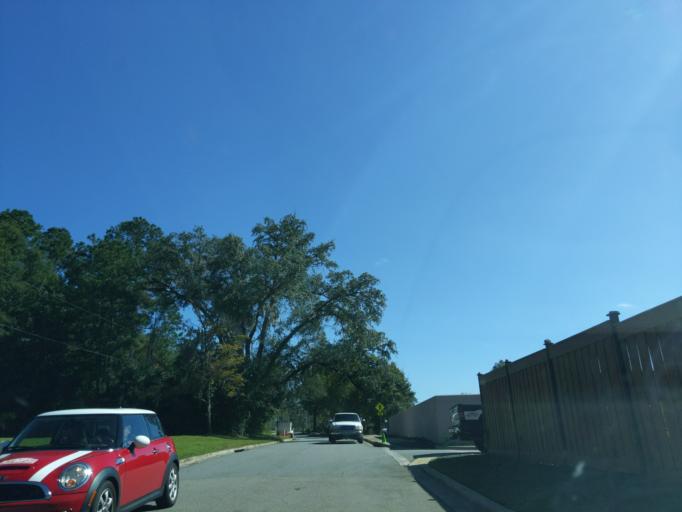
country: US
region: Florida
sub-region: Leon County
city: Tallahassee
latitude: 30.4636
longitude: -84.2310
